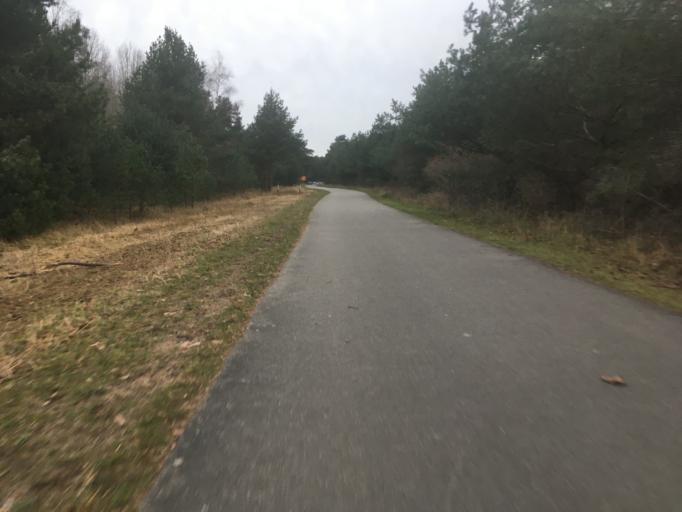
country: DE
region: Mecklenburg-Vorpommern
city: Sagard
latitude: 54.4630
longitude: 13.5663
